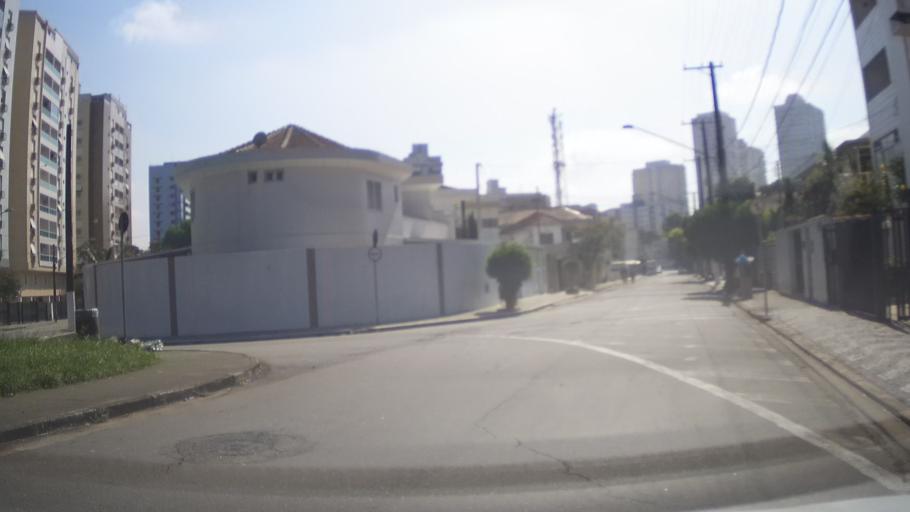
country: BR
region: Sao Paulo
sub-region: Santos
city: Santos
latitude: -23.9880
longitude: -46.3054
